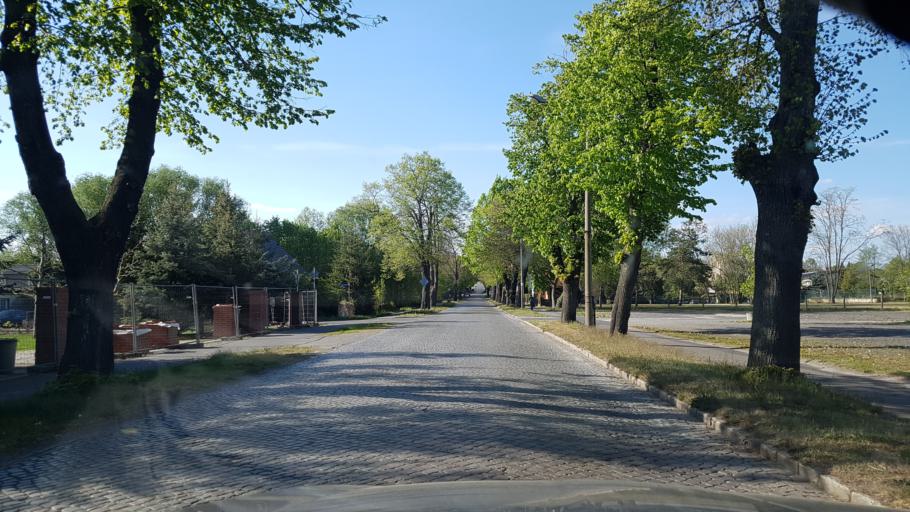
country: DE
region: Brandenburg
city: Elsterwerda
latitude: 51.4677
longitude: 13.5148
